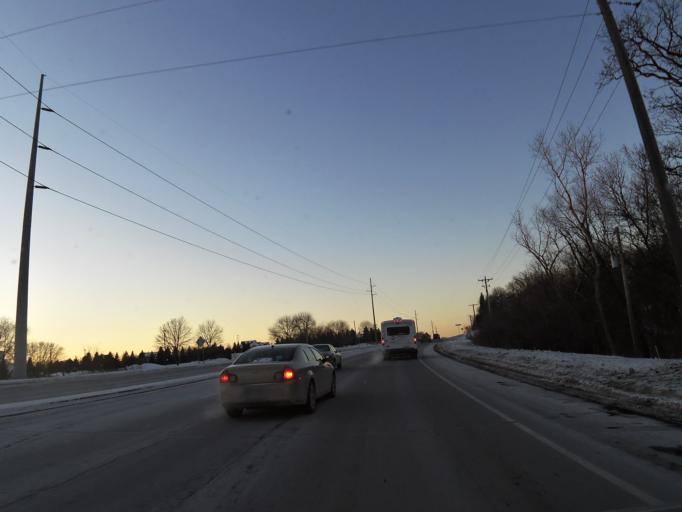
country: US
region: Minnesota
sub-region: Dakota County
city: Apple Valley
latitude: 44.7329
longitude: -93.2523
